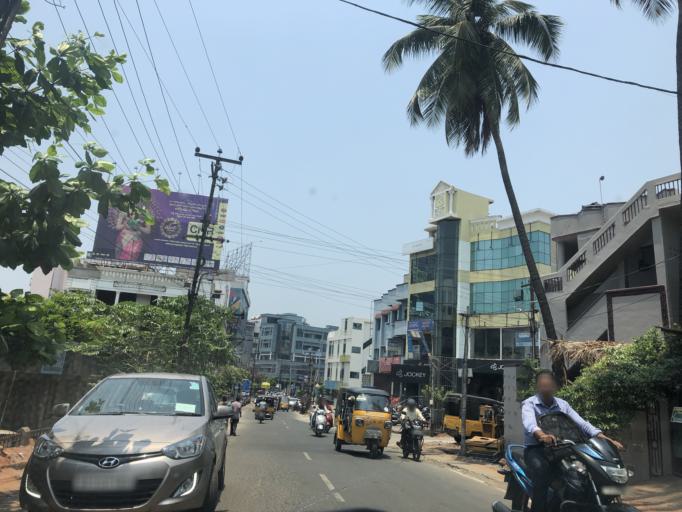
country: IN
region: Andhra Pradesh
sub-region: Vishakhapatnam
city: Yarada
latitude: 17.7144
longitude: 83.3028
